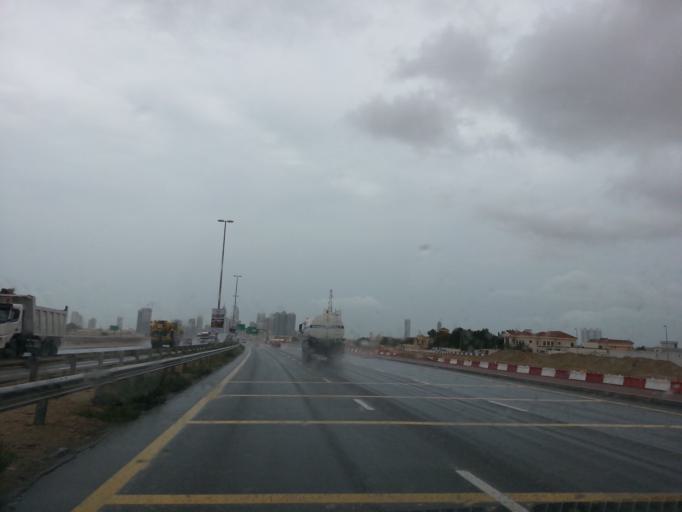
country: AE
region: Dubai
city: Dubai
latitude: 25.0813
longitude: 55.2041
